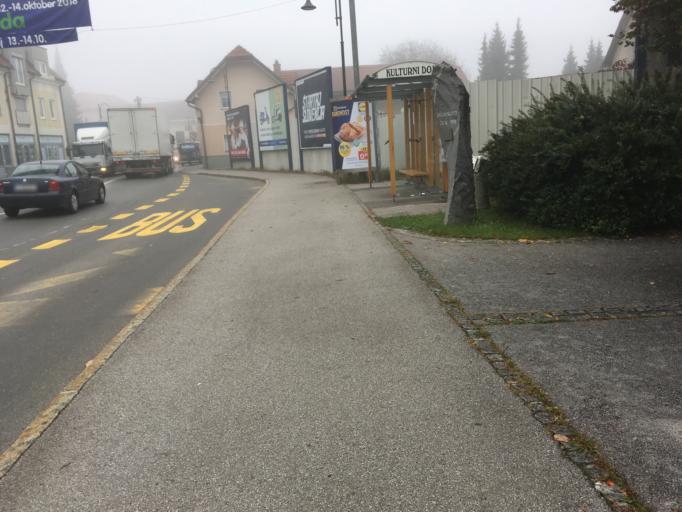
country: SI
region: Menges
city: Menges
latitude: 46.1640
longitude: 14.5713
